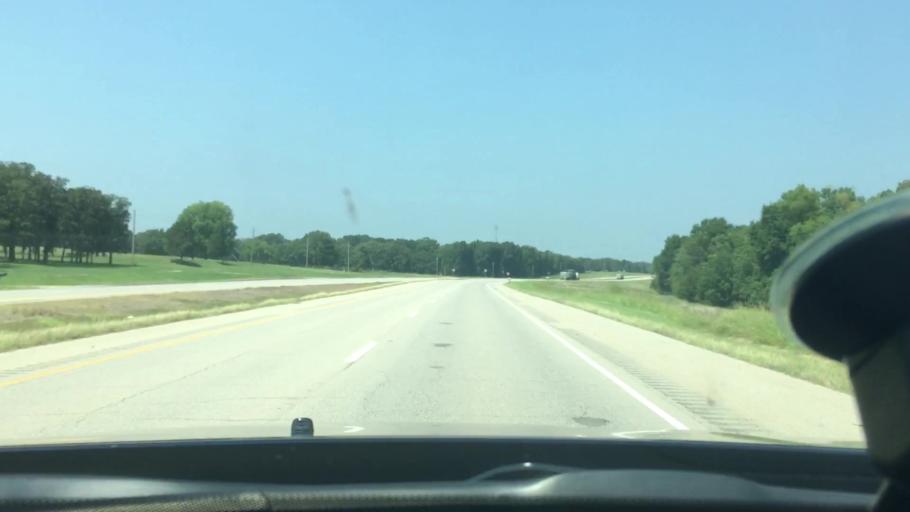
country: US
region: Oklahoma
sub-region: Atoka County
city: Atoka
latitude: 34.3156
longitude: -96.0289
